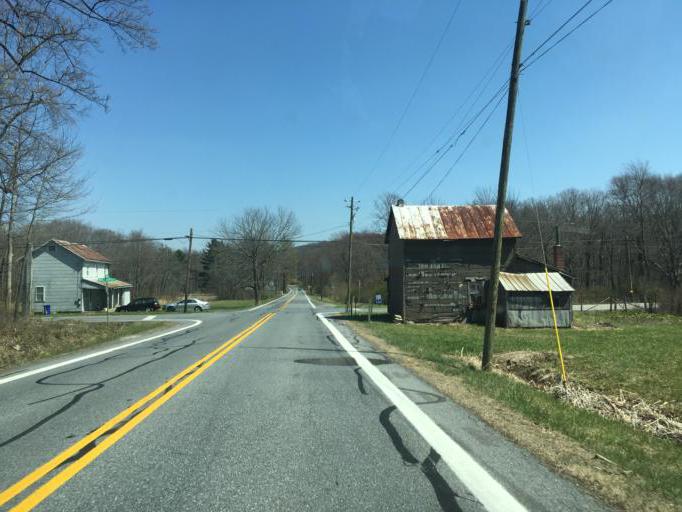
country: US
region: Maryland
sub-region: Washington County
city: Smithsburg
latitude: 39.6363
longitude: -77.4976
